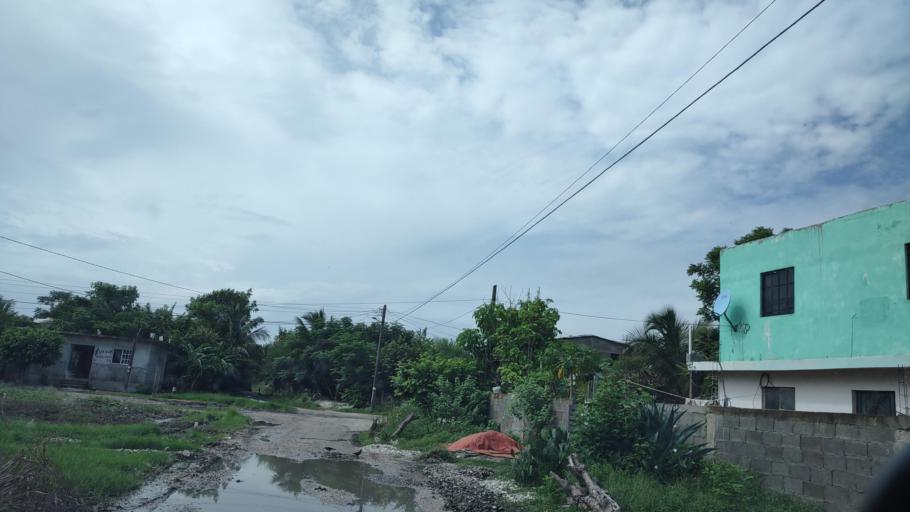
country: MX
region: Veracruz
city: Anahuac
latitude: 22.2064
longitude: -97.8660
